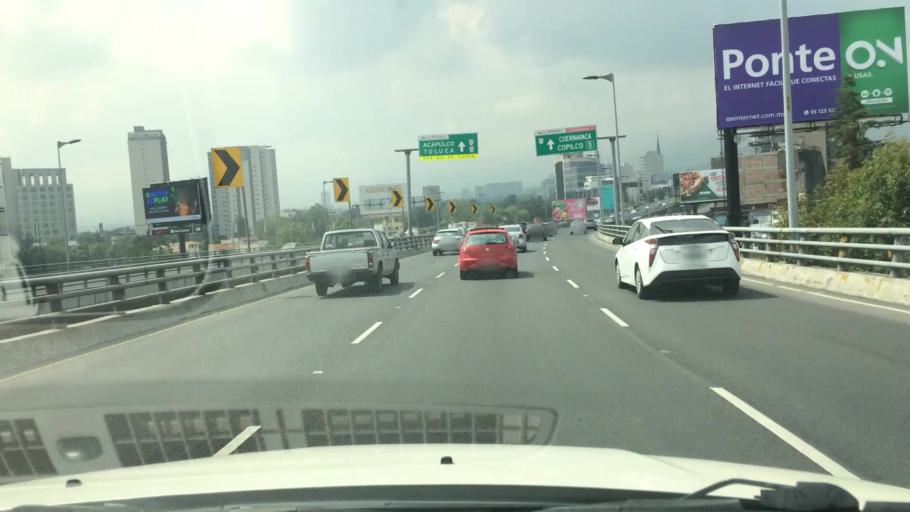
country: MX
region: Mexico City
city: Magdalena Contreras
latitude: 19.3394
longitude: -99.2040
